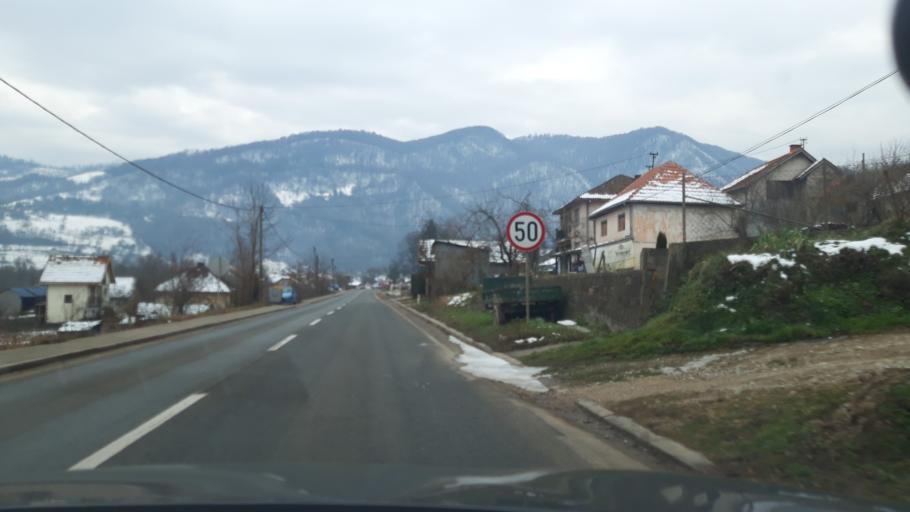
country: RS
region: Central Serbia
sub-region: Macvanski Okrug
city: Mali Zvornik
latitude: 44.2906
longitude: 19.1492
